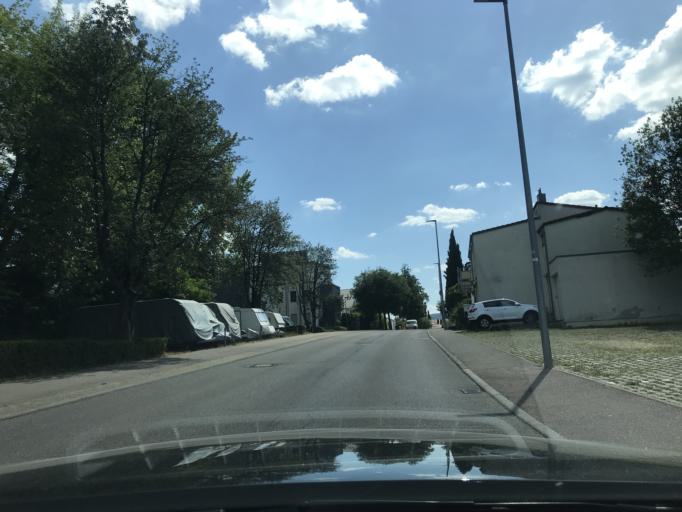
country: DE
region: Baden-Wuerttemberg
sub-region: Regierungsbezirk Stuttgart
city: Weinstadt-Endersbach
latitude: 48.8121
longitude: 9.3735
